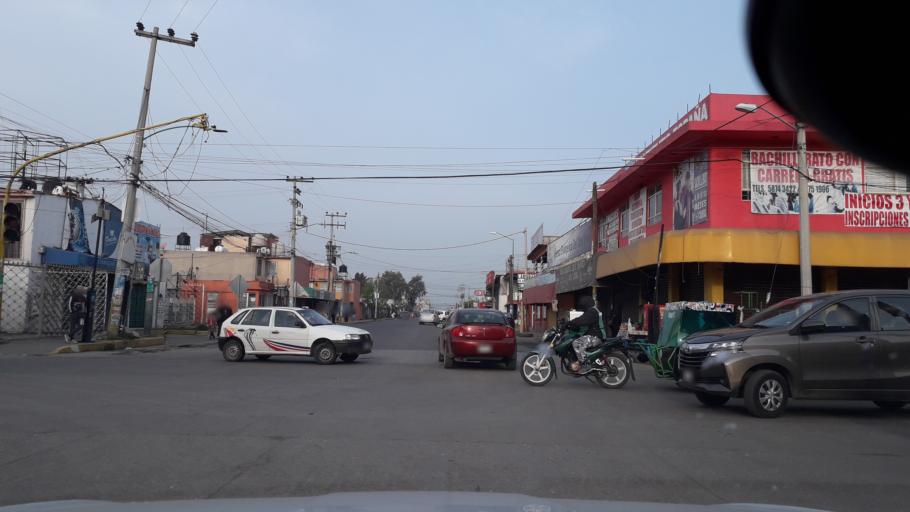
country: MX
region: Mexico
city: San Pablo de las Salinas
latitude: 19.6592
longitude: -99.0832
